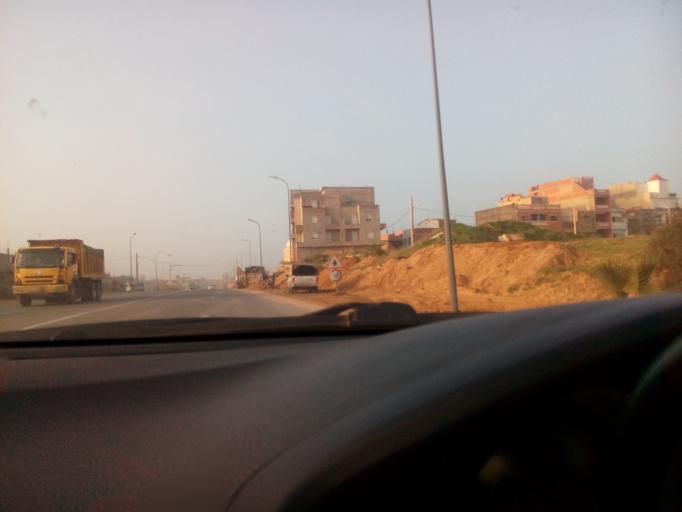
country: DZ
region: Oran
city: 'Ain el Turk
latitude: 35.7256
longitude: -0.8455
